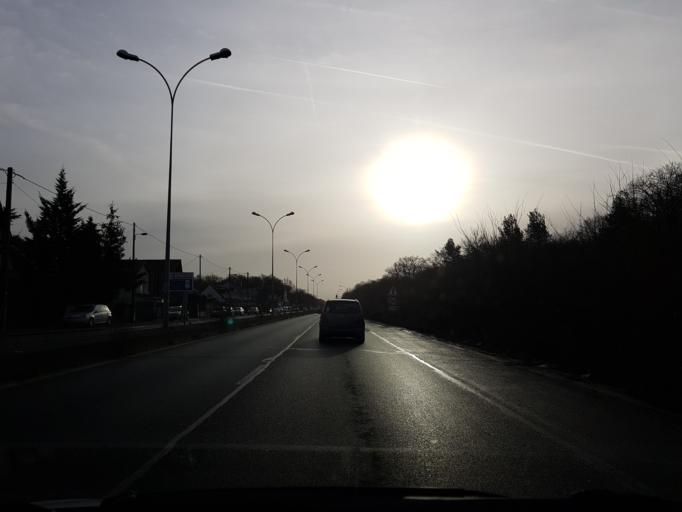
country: FR
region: Ile-de-France
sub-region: Departement de l'Essonne
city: Brunoy
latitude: 48.6802
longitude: 2.4939
